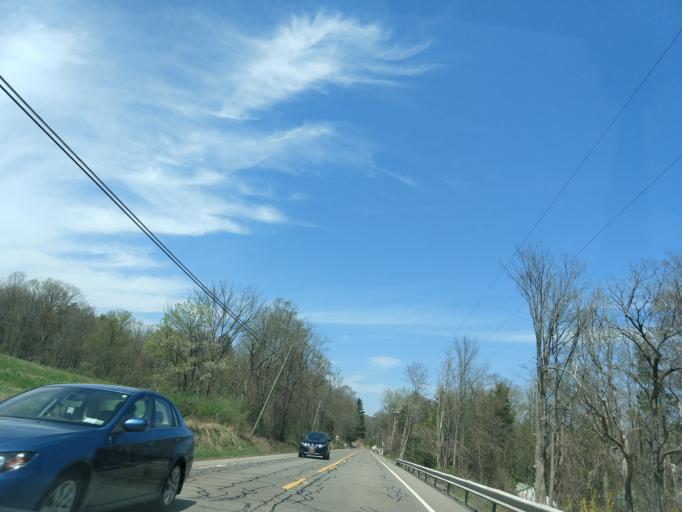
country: US
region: New York
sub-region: Tompkins County
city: Trumansburg
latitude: 42.5365
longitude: -76.5865
